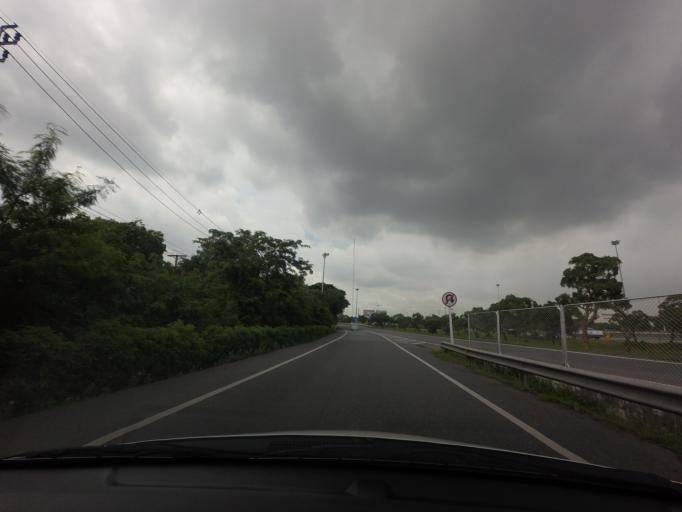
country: TH
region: Bangkok
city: Saphan Sung
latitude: 13.7786
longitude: 100.6861
